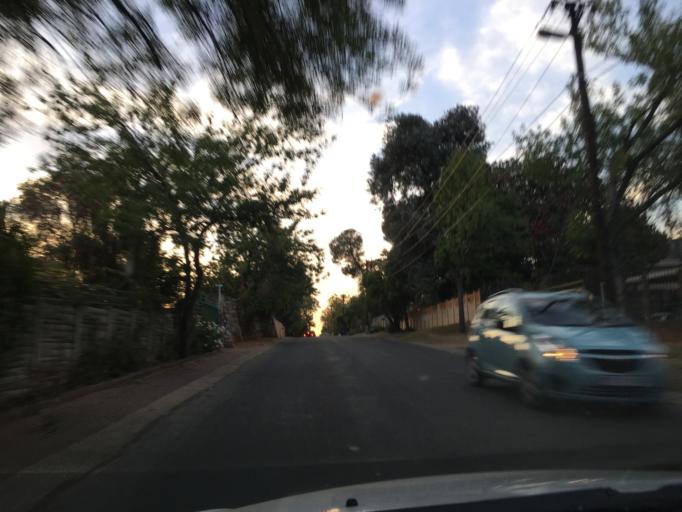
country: ZA
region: Gauteng
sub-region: City of Johannesburg Metropolitan Municipality
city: Johannesburg
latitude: -26.0806
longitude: 28.0072
